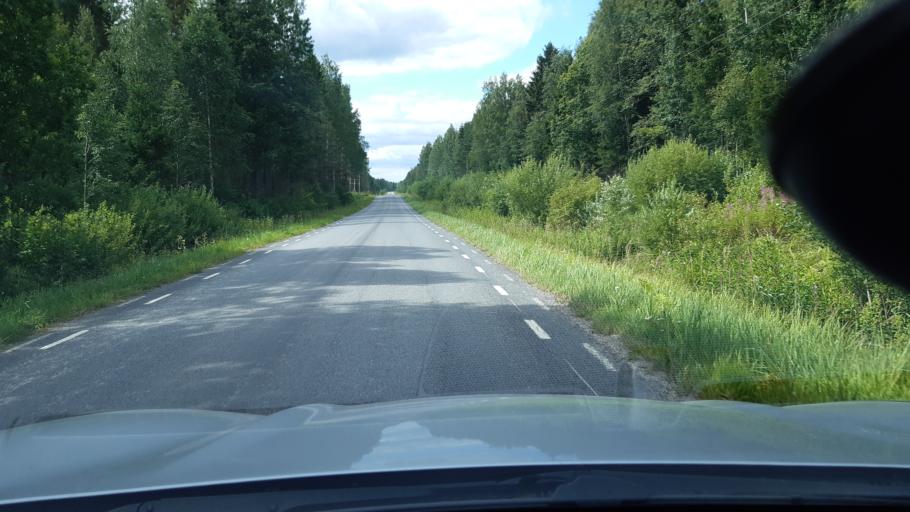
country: EE
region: Raplamaa
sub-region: Jaervakandi vald
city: Jarvakandi
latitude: 58.8001
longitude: 24.8997
